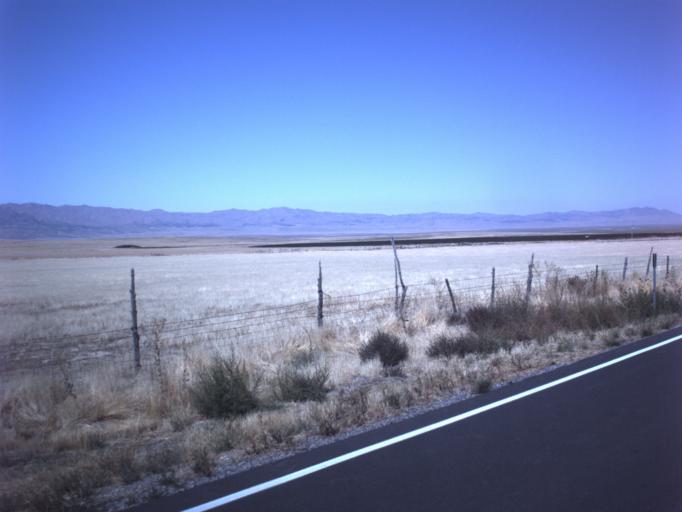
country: US
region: Utah
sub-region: Tooele County
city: Grantsville
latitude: 40.4281
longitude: -112.7487
